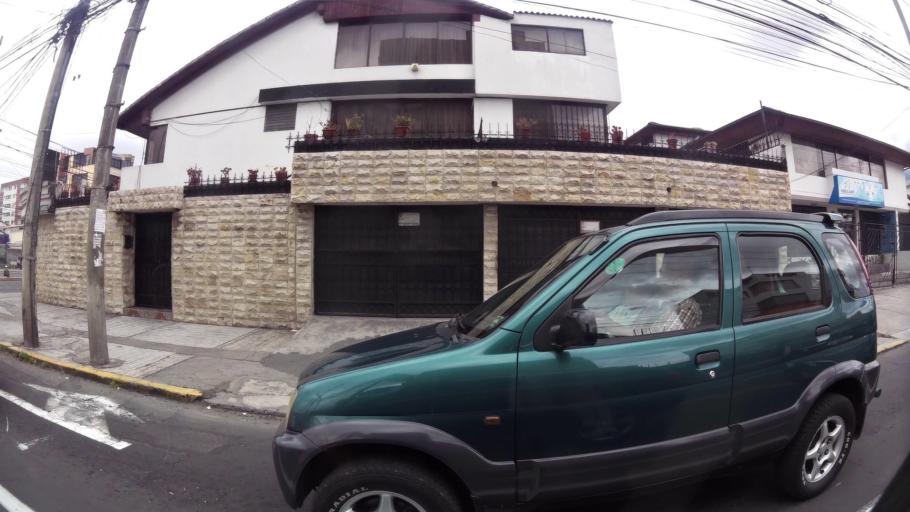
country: EC
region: Pichincha
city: Quito
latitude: -0.1628
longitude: -78.4788
